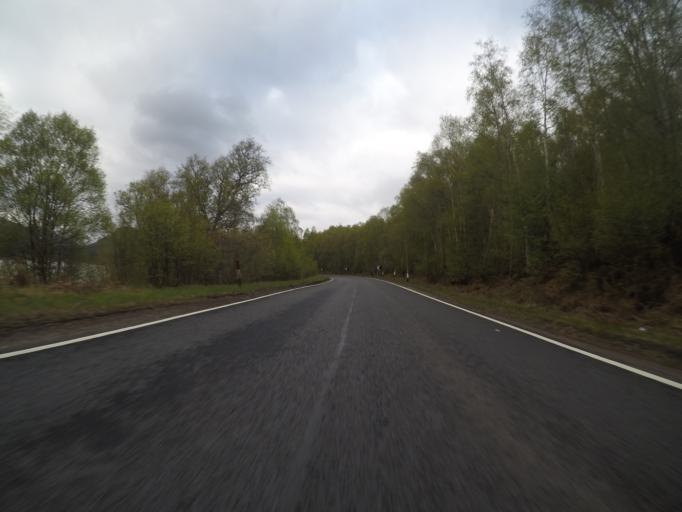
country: GB
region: Scotland
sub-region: Highland
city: Kingussie
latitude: 56.9668
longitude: -4.4424
